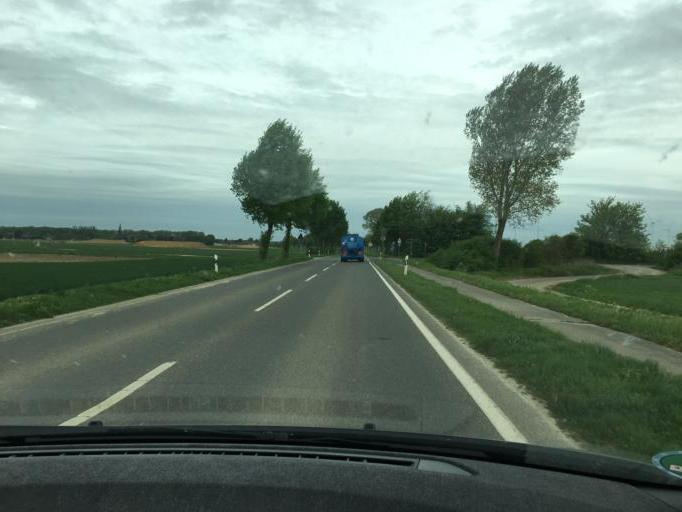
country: DE
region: North Rhine-Westphalia
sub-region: Regierungsbezirk Koln
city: Titz
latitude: 51.0740
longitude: 6.4257
